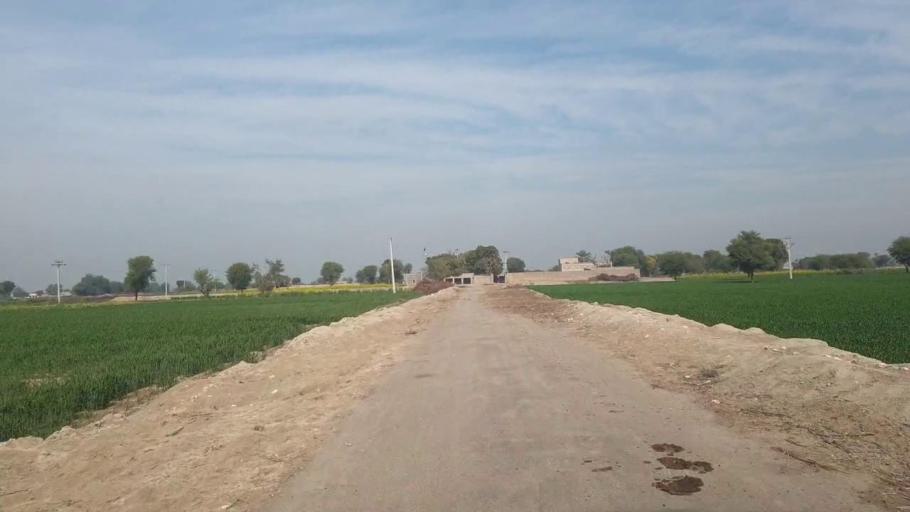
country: PK
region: Sindh
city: Nawabshah
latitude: 26.1548
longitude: 68.5071
